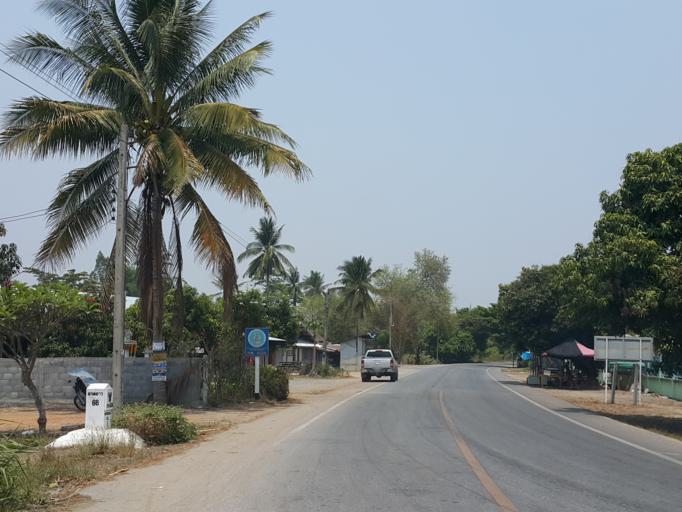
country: TH
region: Kamphaeng Phet
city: Pang Sila Thong
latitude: 16.0568
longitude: 99.3776
